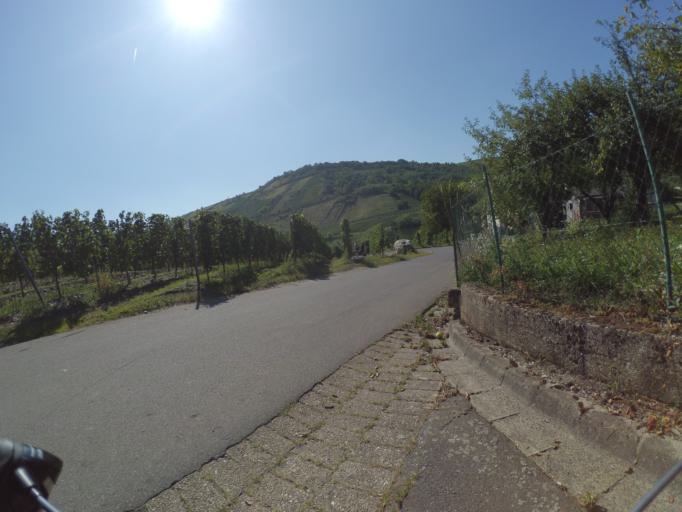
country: DE
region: Rheinland-Pfalz
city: Neumagen-Dhron
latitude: 49.8435
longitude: 6.8961
